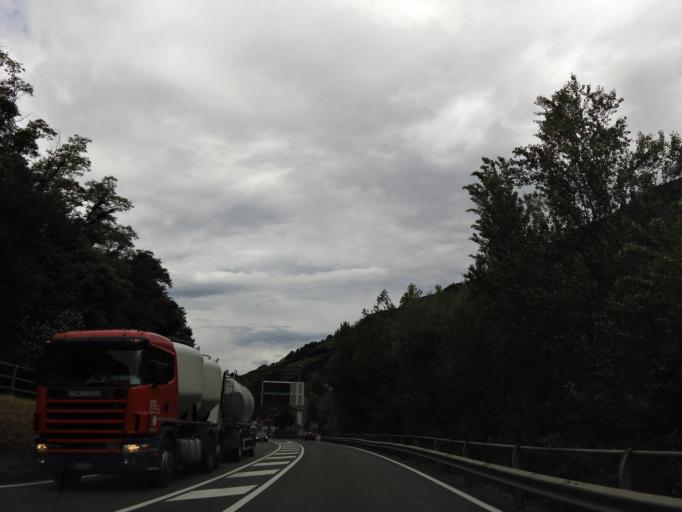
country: IT
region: Trentino-Alto Adige
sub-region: Bolzano
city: Cornedo All'Isarco
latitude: 46.4928
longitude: 11.4135
